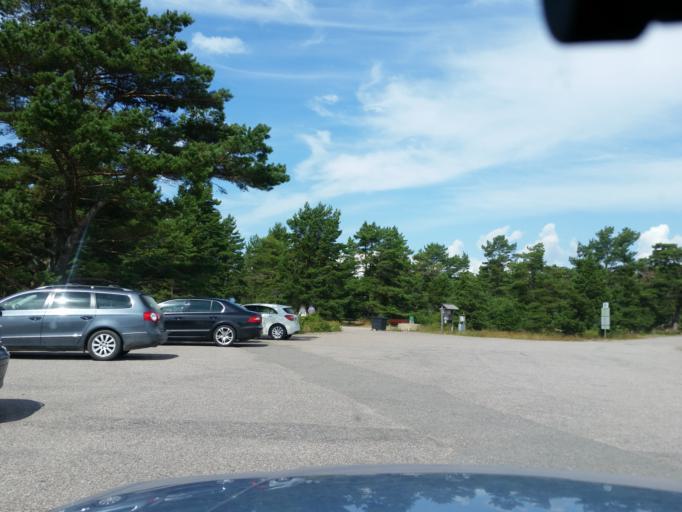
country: FI
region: Uusimaa
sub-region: Raaseporin
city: Hanko
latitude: 59.8245
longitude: 23.0075
